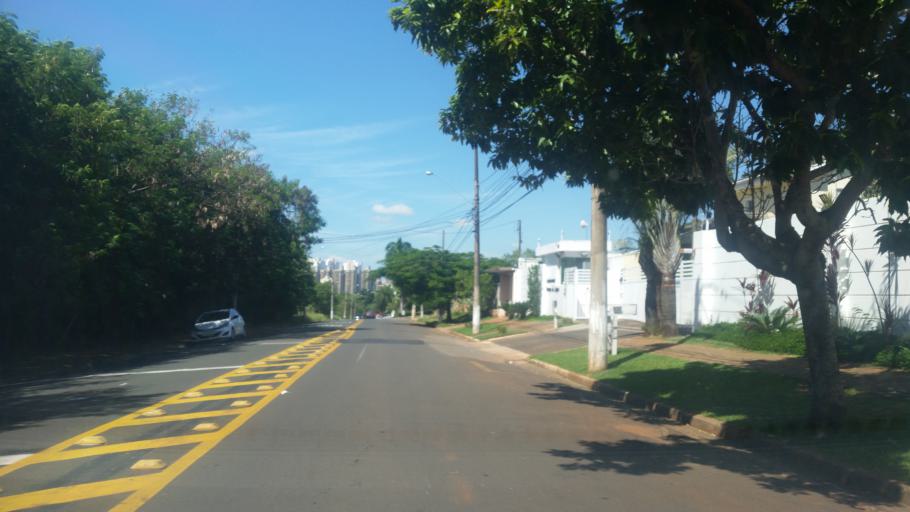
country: BR
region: Sao Paulo
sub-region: Campinas
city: Campinas
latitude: -22.8669
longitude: -47.0489
